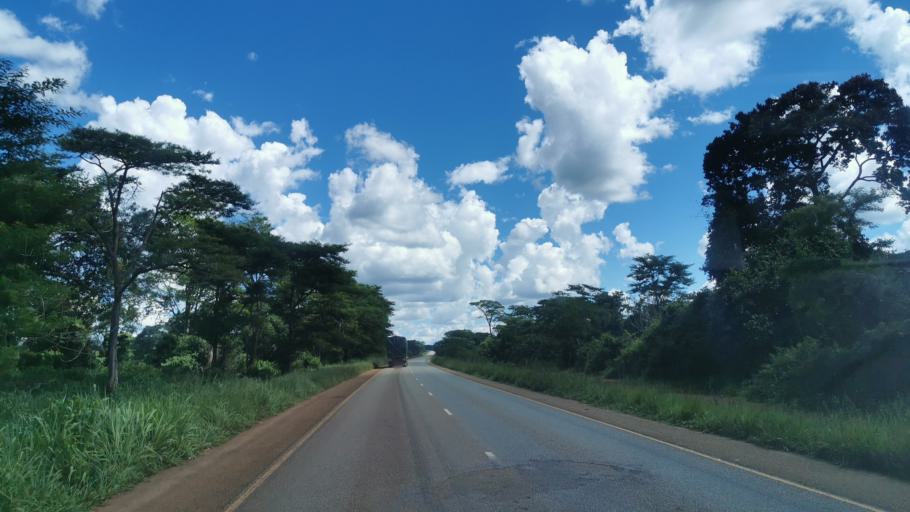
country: TZ
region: Geita
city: Uyovu
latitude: -3.0520
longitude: 31.2557
